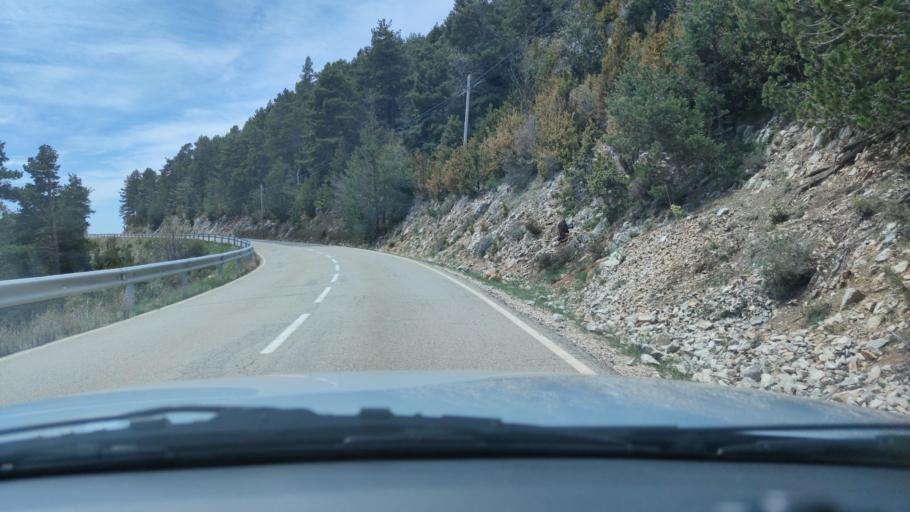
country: ES
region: Catalonia
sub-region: Provincia de Lleida
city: Gosol
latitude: 42.1635
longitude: 1.5752
